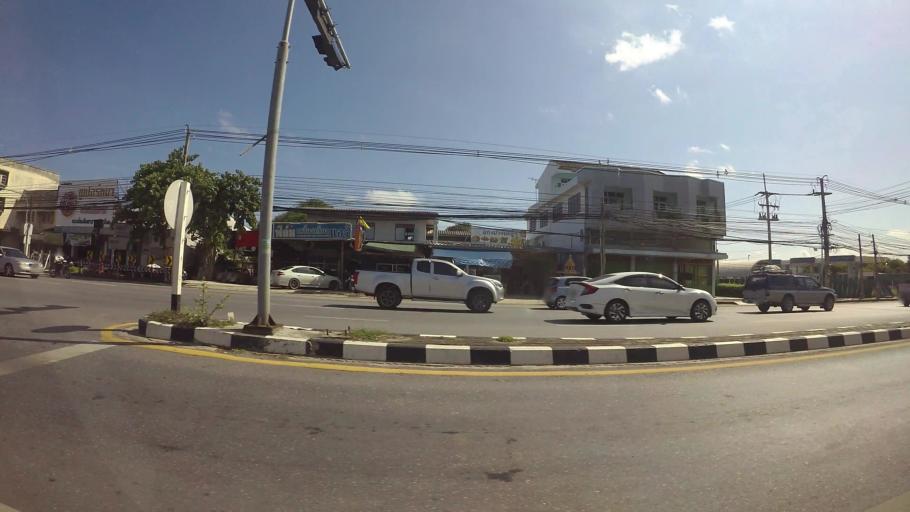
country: TH
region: Rayong
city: Rayong
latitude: 12.6750
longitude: 101.2895
